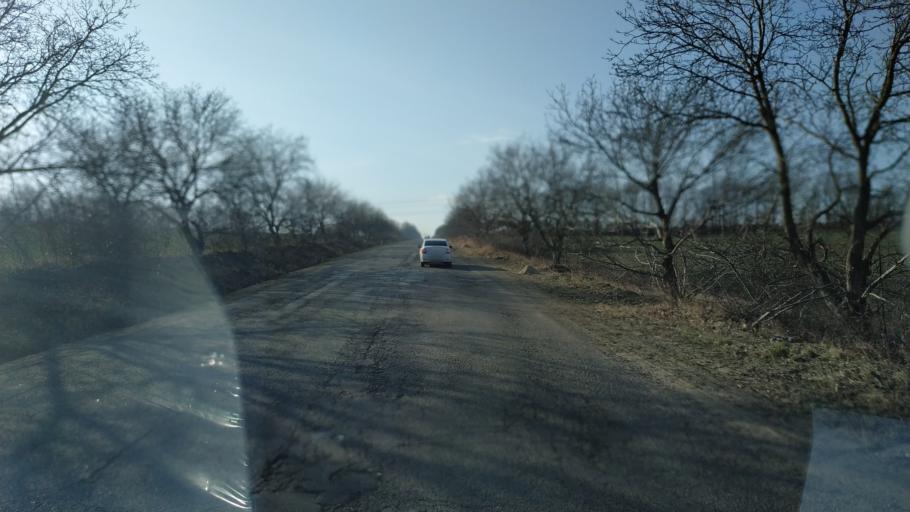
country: MD
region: Chisinau
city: Singera
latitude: 46.8763
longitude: 29.0395
